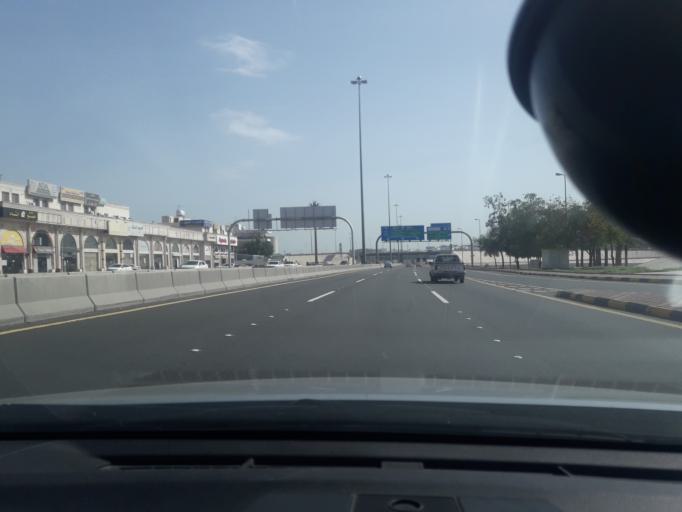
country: SA
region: Al Madinah al Munawwarah
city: Medina
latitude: 24.4410
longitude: 39.6220
